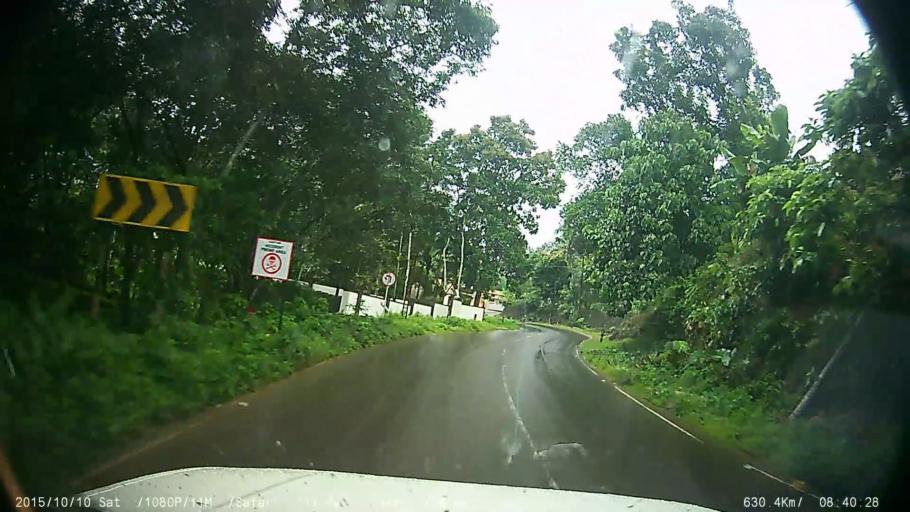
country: IN
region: Kerala
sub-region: Kottayam
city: Palackattumala
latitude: 9.7575
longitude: 76.5506
